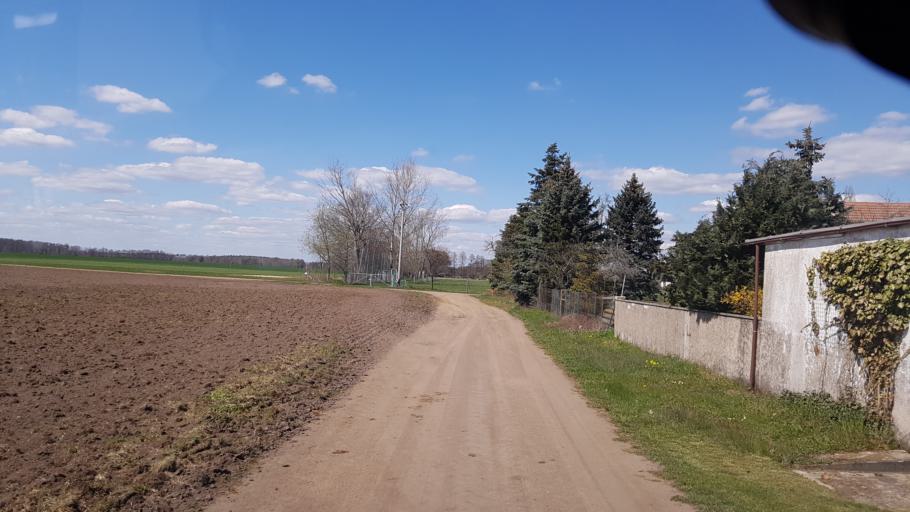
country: DE
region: Brandenburg
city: Bad Liebenwerda
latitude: 51.4880
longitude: 13.3338
